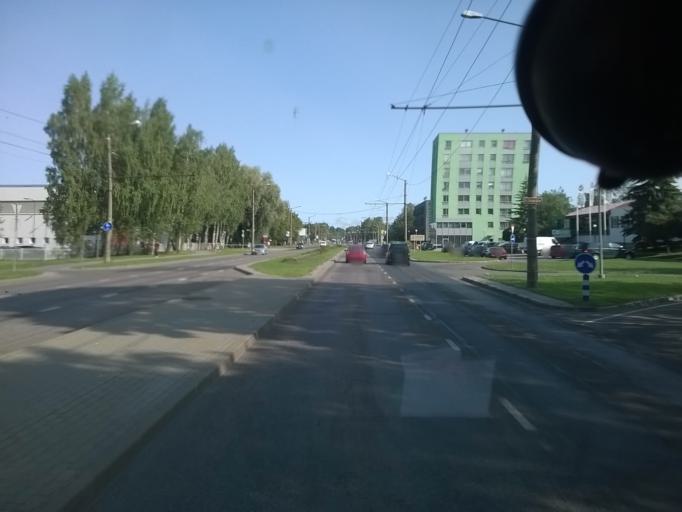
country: EE
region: Harju
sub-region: Tallinna linn
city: Tallinn
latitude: 59.4099
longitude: 24.7053
